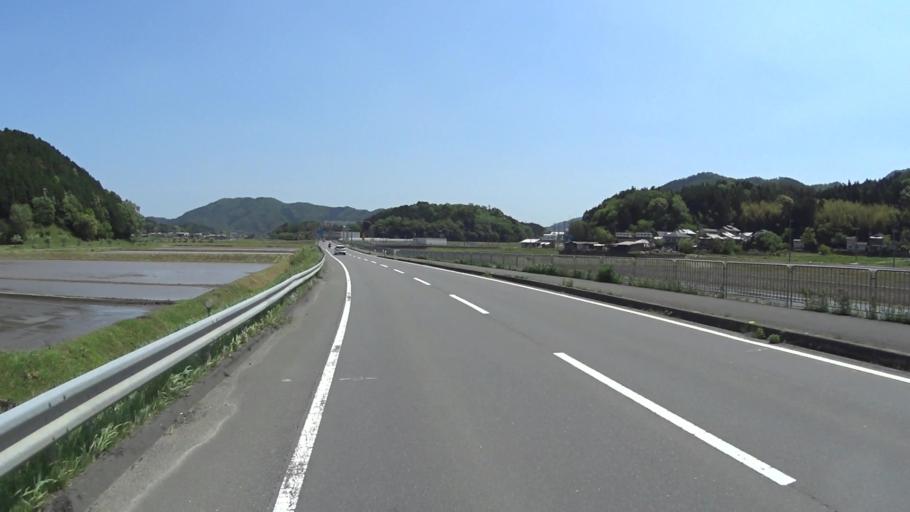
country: JP
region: Kyoto
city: Kameoka
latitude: 35.0384
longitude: 135.4844
